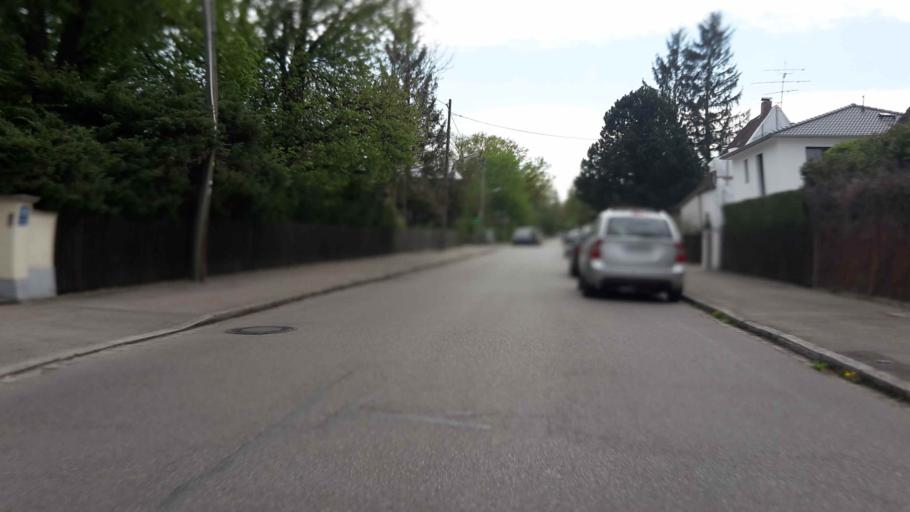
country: DE
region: Bavaria
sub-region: Upper Bavaria
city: Karlsfeld
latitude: 48.1774
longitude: 11.4892
